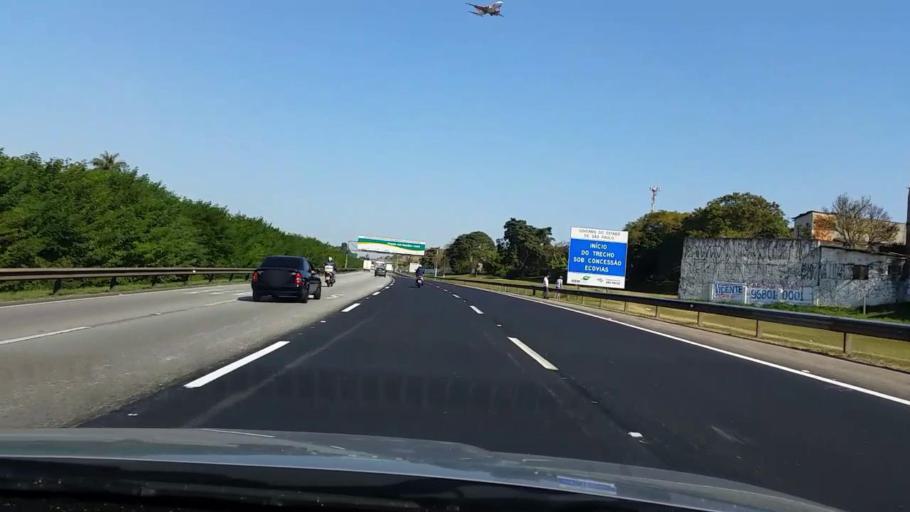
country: BR
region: Sao Paulo
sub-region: Diadema
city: Diadema
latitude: -23.6542
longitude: -46.6343
